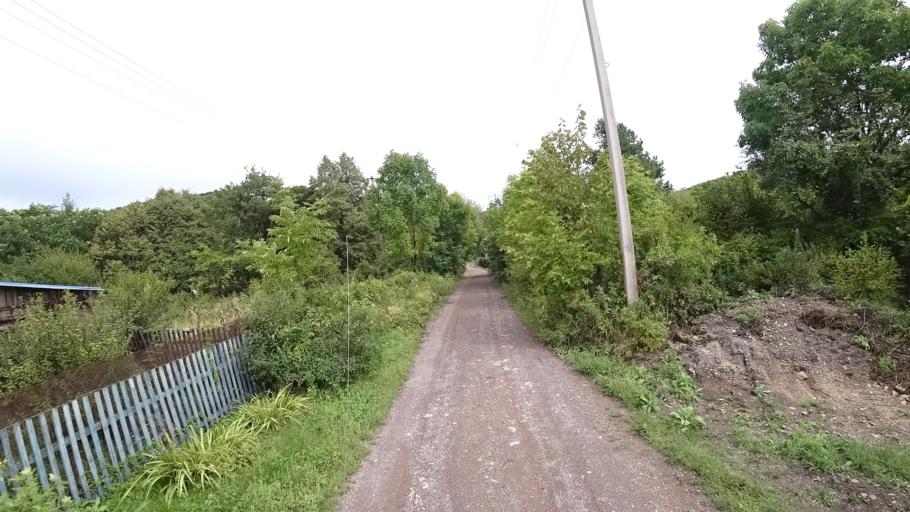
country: RU
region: Primorskiy
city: Monastyrishche
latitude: 44.1659
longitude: 132.5407
